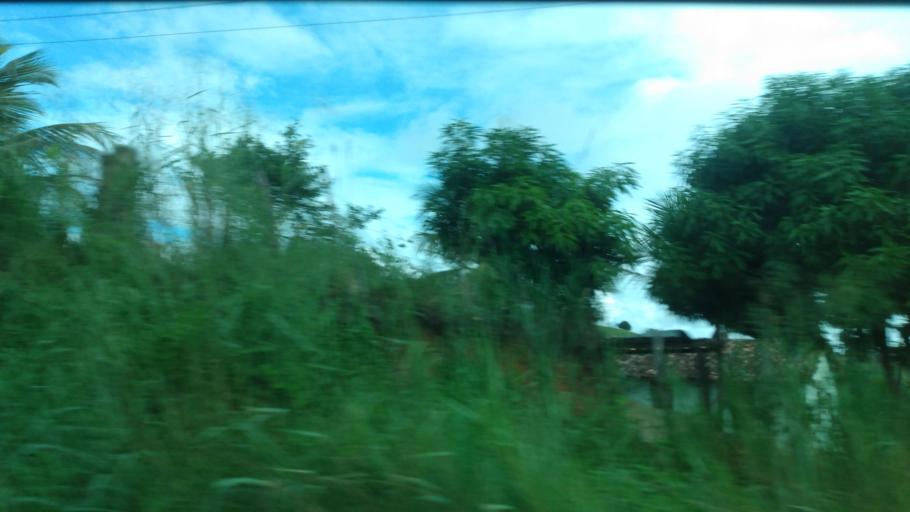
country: BR
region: Pernambuco
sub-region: Catende
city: Catende
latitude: -8.6923
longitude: -35.7184
